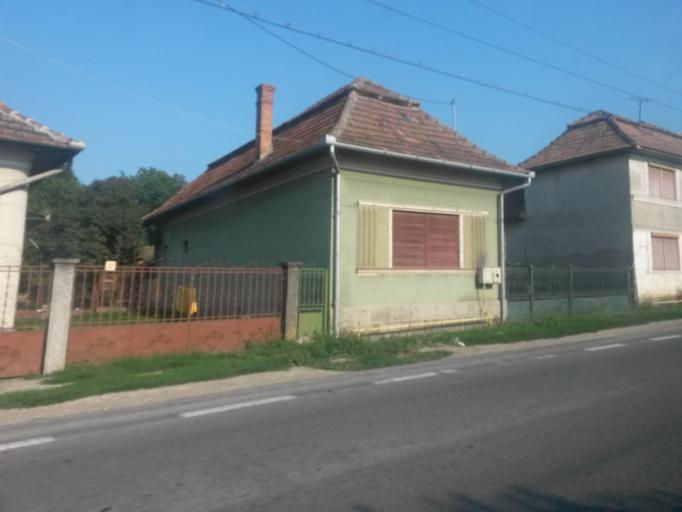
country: RO
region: Alba
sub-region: Comuna Unirea
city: Unirea
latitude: 46.4075
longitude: 23.8106
